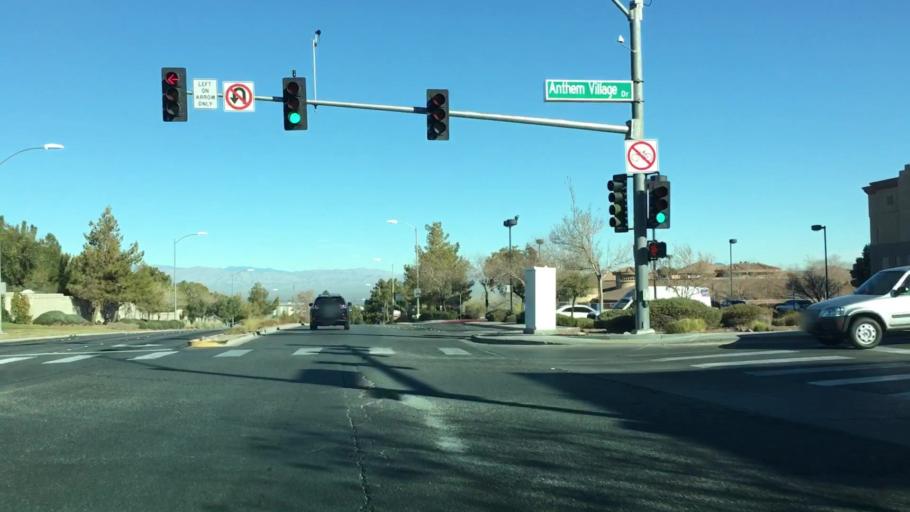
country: US
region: Nevada
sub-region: Clark County
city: Whitney
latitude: 35.9802
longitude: -115.1008
